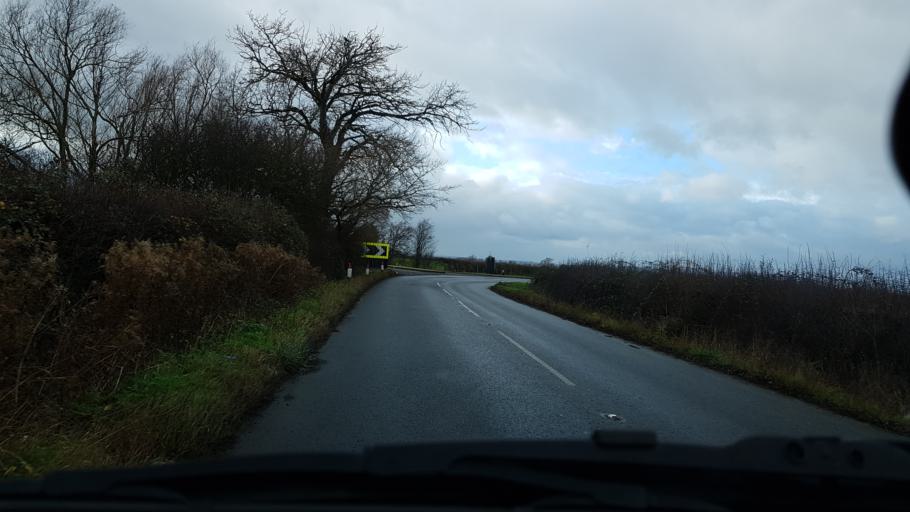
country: GB
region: England
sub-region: Gloucestershire
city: Gotherington
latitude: 51.9874
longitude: -2.0761
